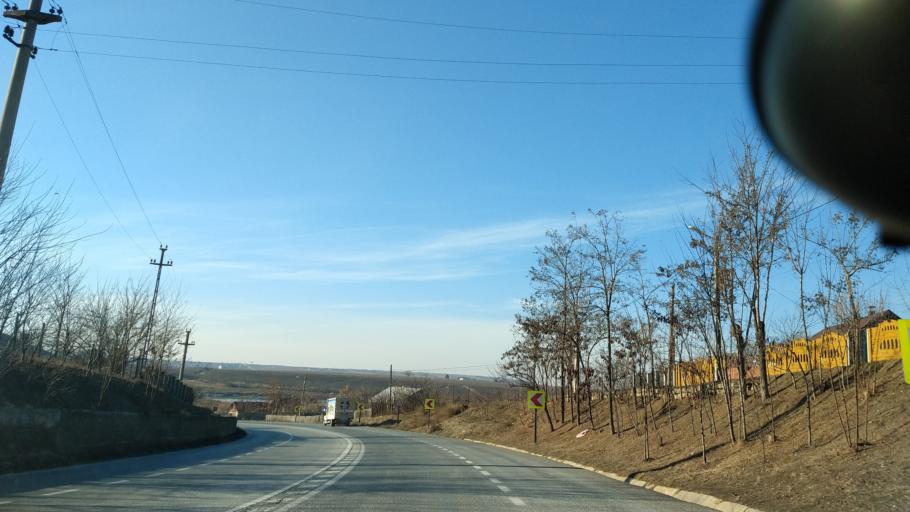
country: RO
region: Iasi
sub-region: Comuna Baltati
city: Baltati
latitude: 47.2254
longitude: 27.1828
